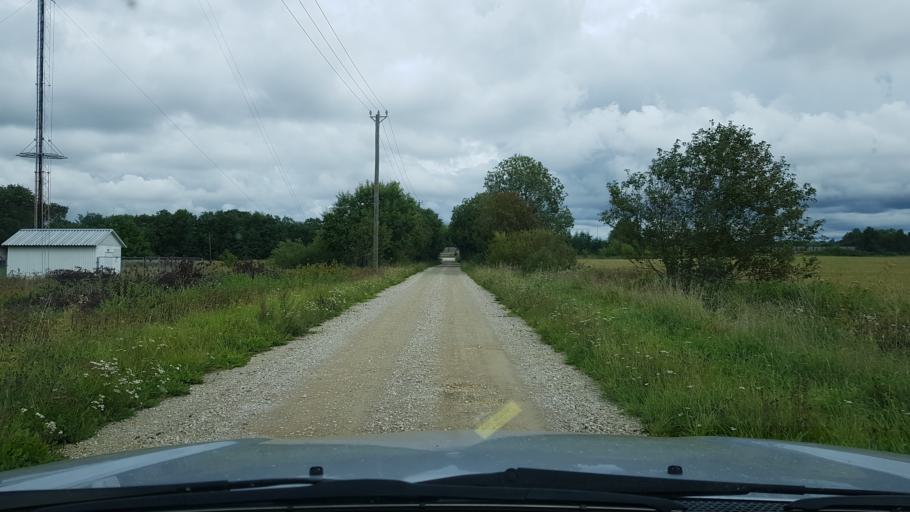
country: EE
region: Harju
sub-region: Rae vald
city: Vaida
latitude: 59.2792
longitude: 24.9736
